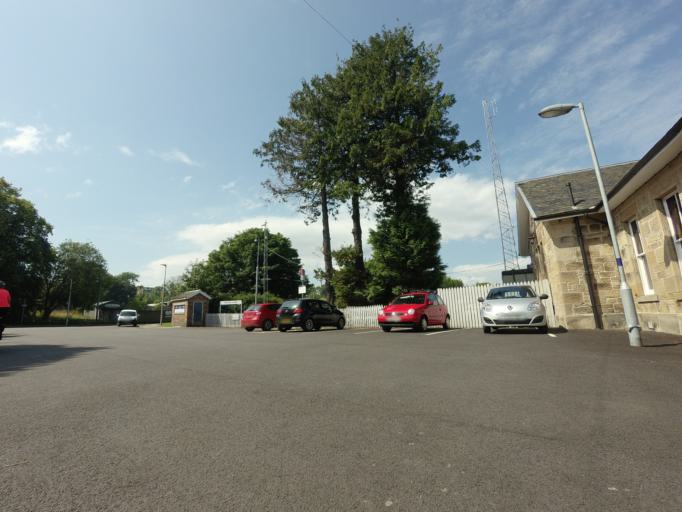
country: GB
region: Scotland
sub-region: Highland
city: Tain
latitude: 57.8141
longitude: -4.0522
